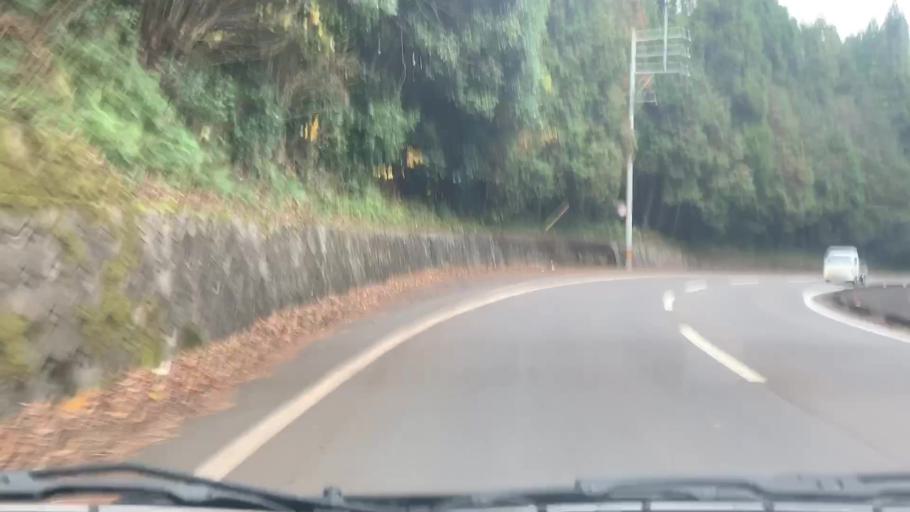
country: JP
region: Saga Prefecture
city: Takeocho-takeo
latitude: 33.2089
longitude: 129.9630
